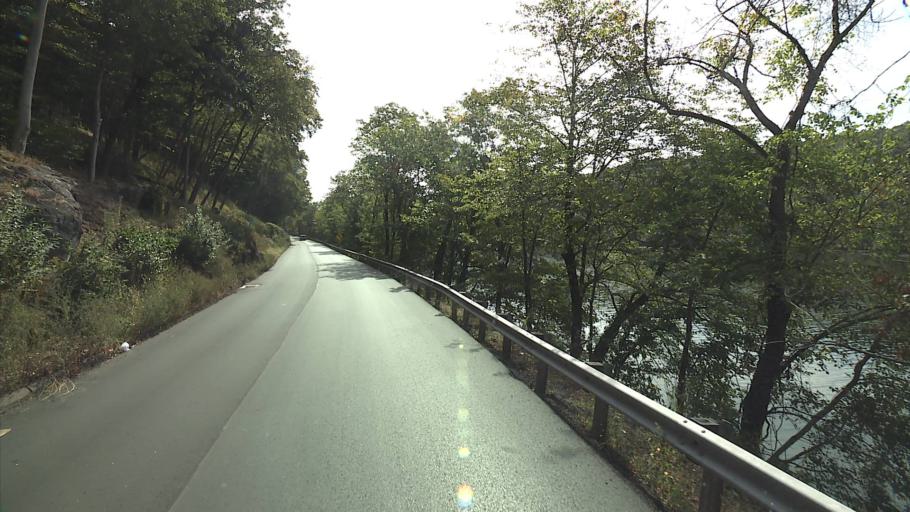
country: US
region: Connecticut
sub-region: Fairfield County
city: Shelton
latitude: 41.3341
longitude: -73.1159
